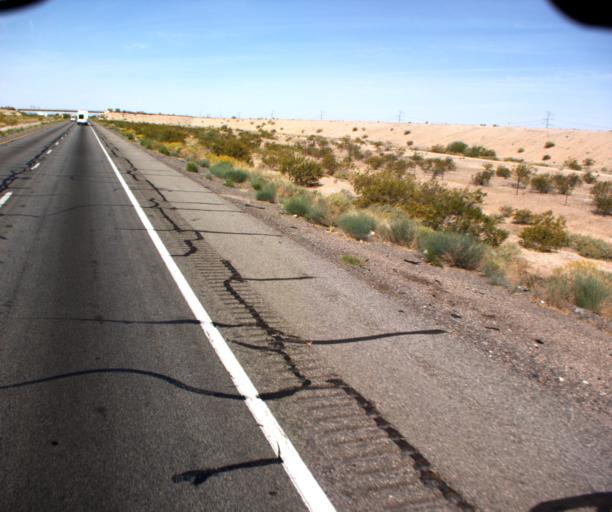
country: US
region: Arizona
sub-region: Maricopa County
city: Buckeye
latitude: 33.4459
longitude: -112.7060
